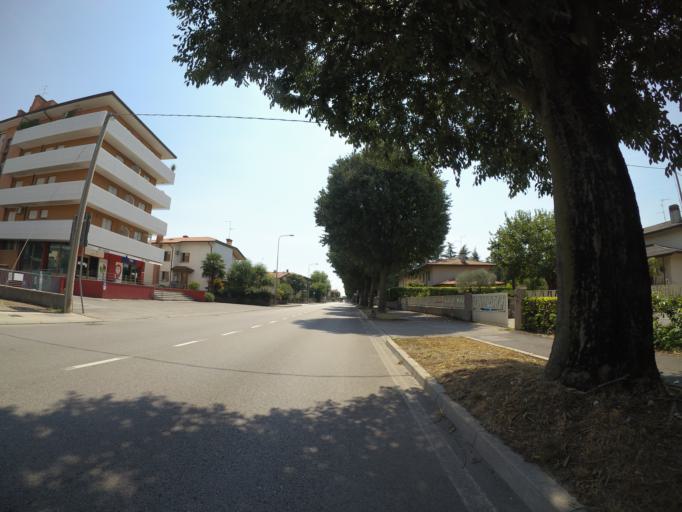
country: IT
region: Friuli Venezia Giulia
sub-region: Provincia di Udine
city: Codroipo
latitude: 45.9615
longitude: 12.9725
